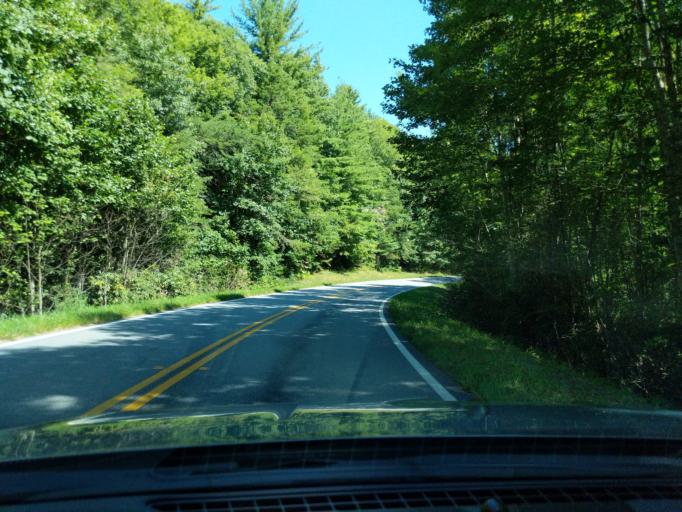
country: US
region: Georgia
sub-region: Towns County
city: Hiawassee
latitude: 34.8499
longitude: -83.7984
